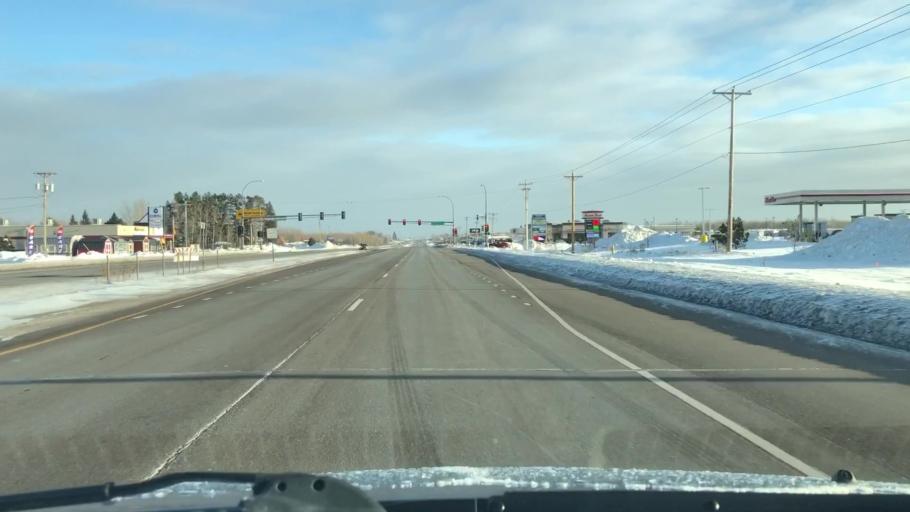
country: US
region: Minnesota
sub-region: Saint Louis County
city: Hermantown
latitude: 46.8345
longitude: -92.2071
